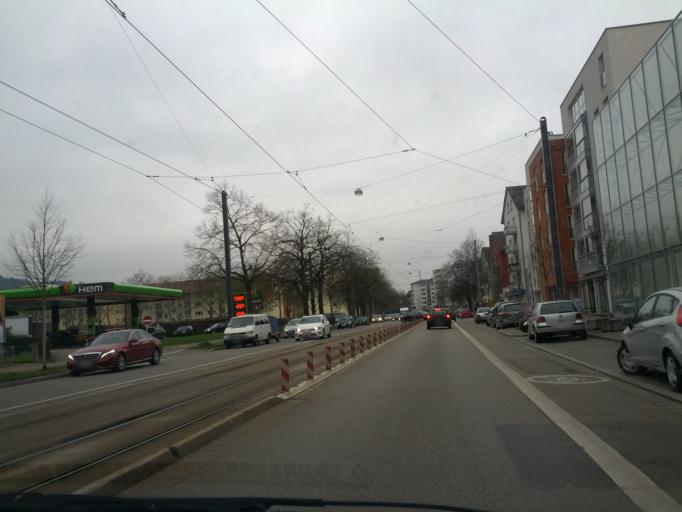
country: DE
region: Baden-Wuerttemberg
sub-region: Freiburg Region
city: Freiburg
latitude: 48.0178
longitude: 7.8562
